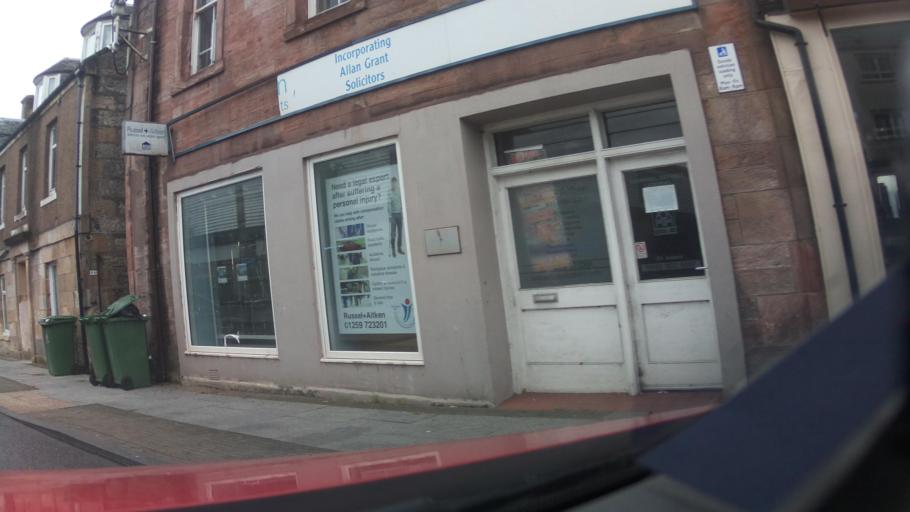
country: GB
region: Scotland
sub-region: Clackmannanshire
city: Alloa
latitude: 56.1159
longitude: -3.7891
